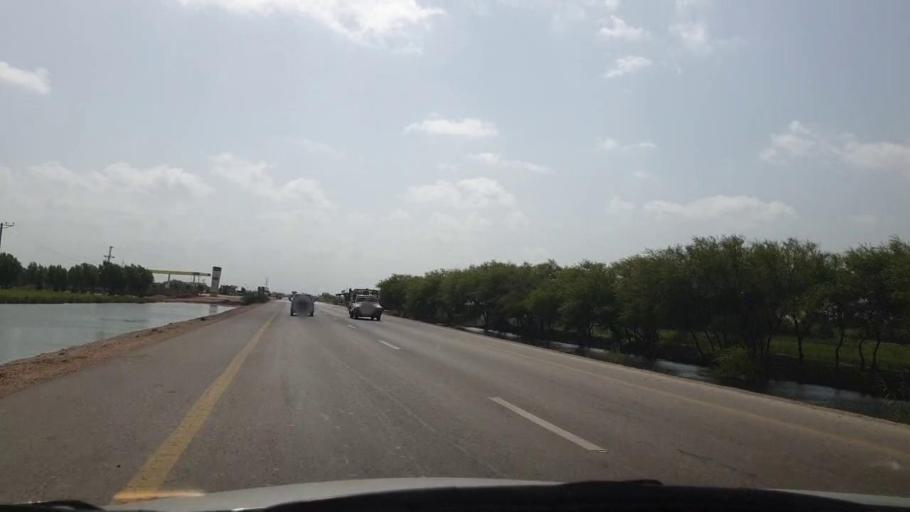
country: PK
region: Sindh
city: Talhar
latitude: 24.9319
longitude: 68.7123
